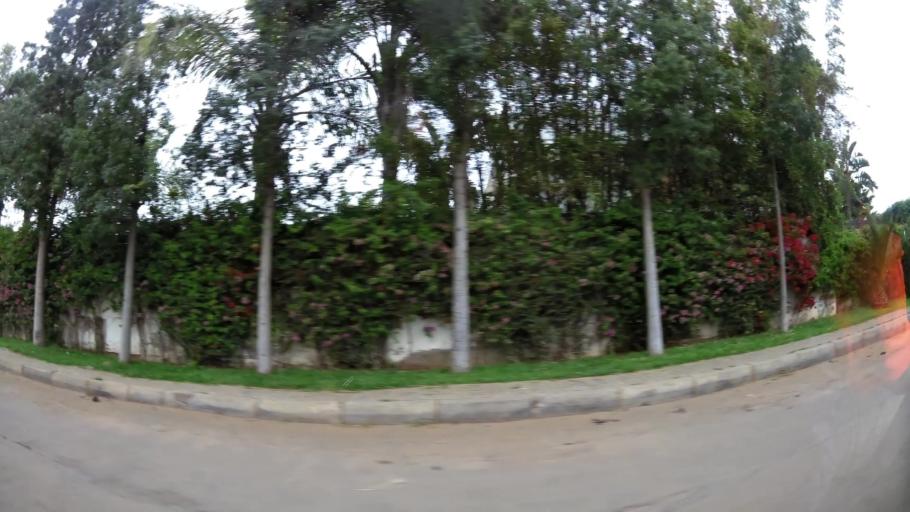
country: MA
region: Grand Casablanca
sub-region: Casablanca
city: Casablanca
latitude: 33.5415
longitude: -7.6337
